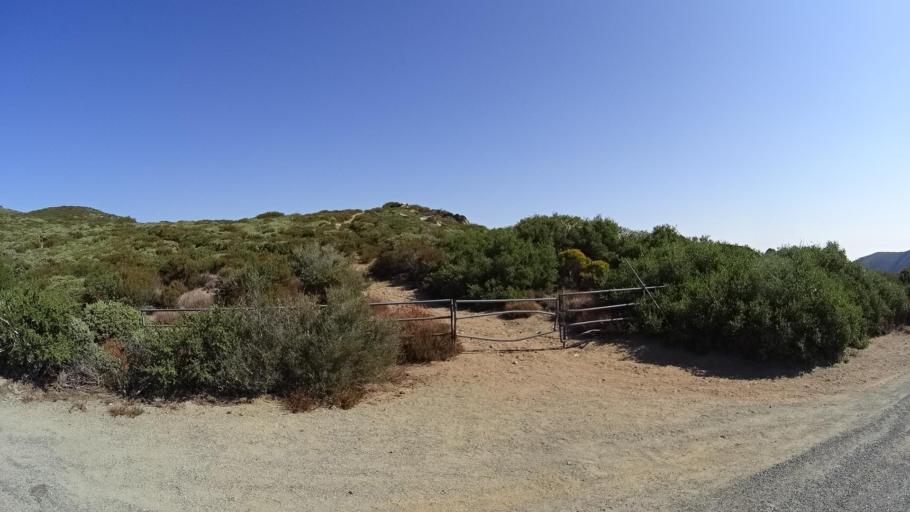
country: US
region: California
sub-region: San Diego County
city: Pine Valley
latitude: 32.9348
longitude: -116.4828
